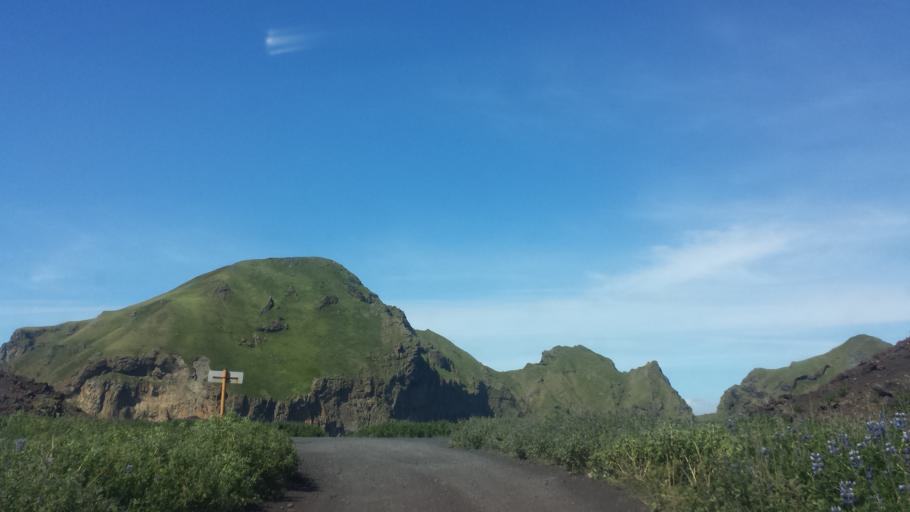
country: IS
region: South
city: Vestmannaeyjar
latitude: 63.4413
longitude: -20.2491
